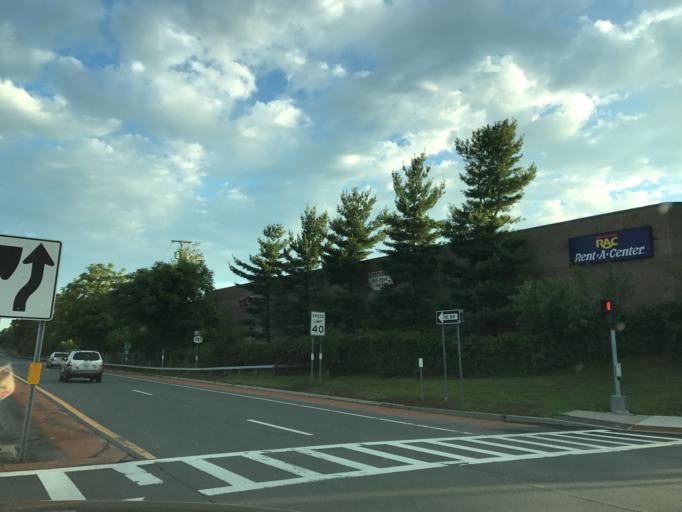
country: US
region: New York
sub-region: Albany County
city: Cohoes
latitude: 42.7740
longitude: -73.6967
